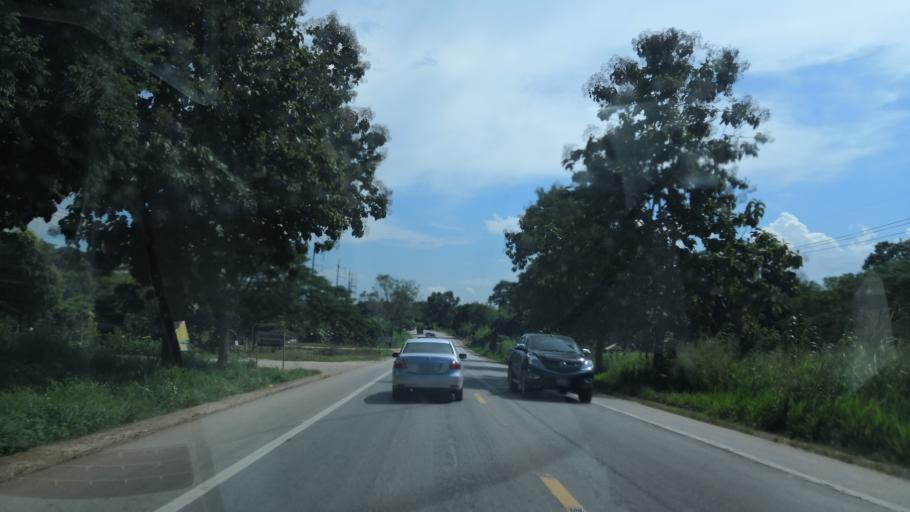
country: TH
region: Chiang Rai
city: Wiang Pa Pao
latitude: 19.4076
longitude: 99.5005
